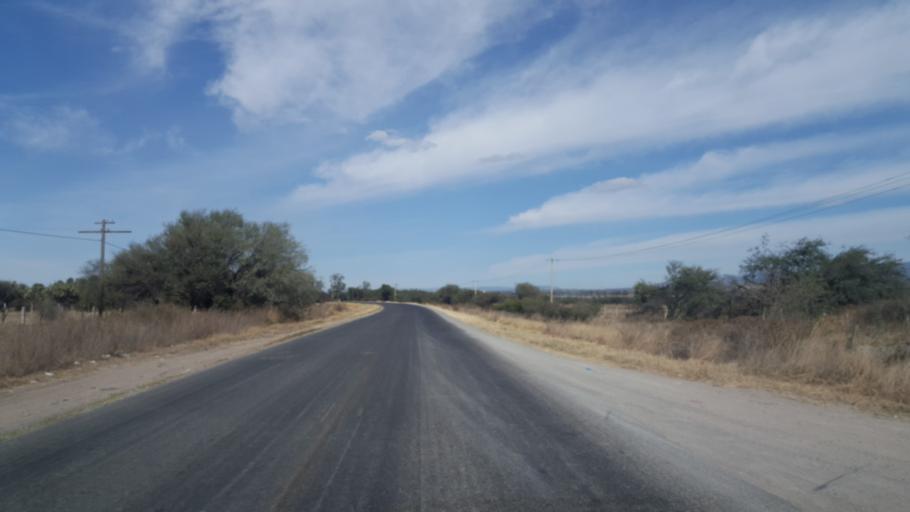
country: MX
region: Jalisco
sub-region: Lagos de Moreno
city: Geovillas Laureles del Campanario
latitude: 21.2935
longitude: -101.9298
